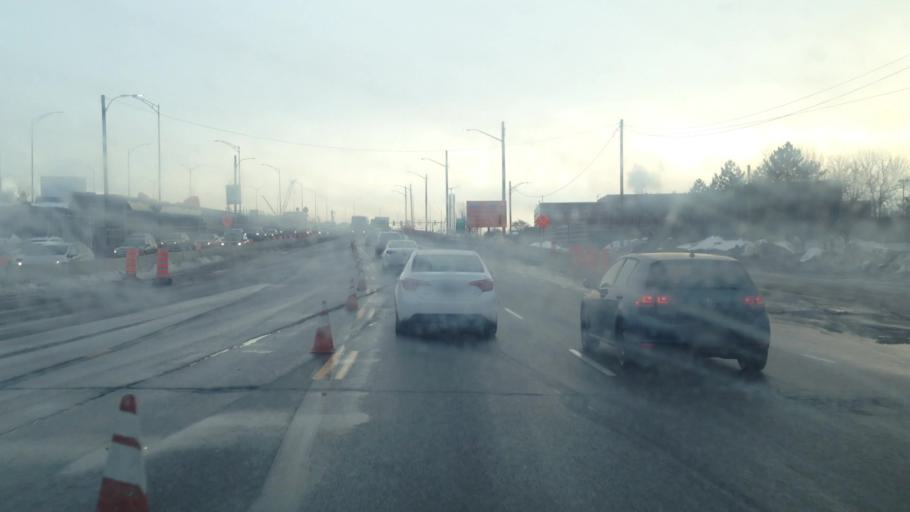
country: CA
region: Quebec
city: Westmount
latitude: 45.4698
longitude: -73.5394
